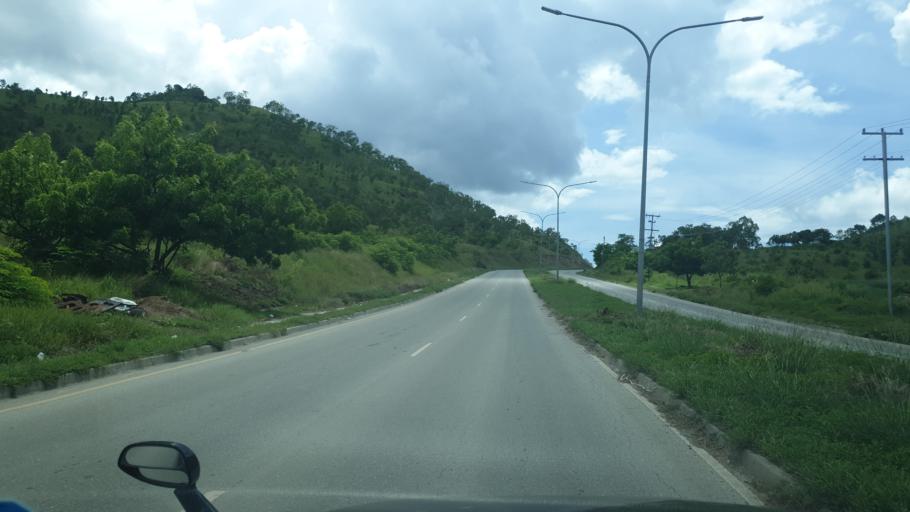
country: PG
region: National Capital
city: Port Moresby
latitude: -9.4213
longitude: 147.1380
